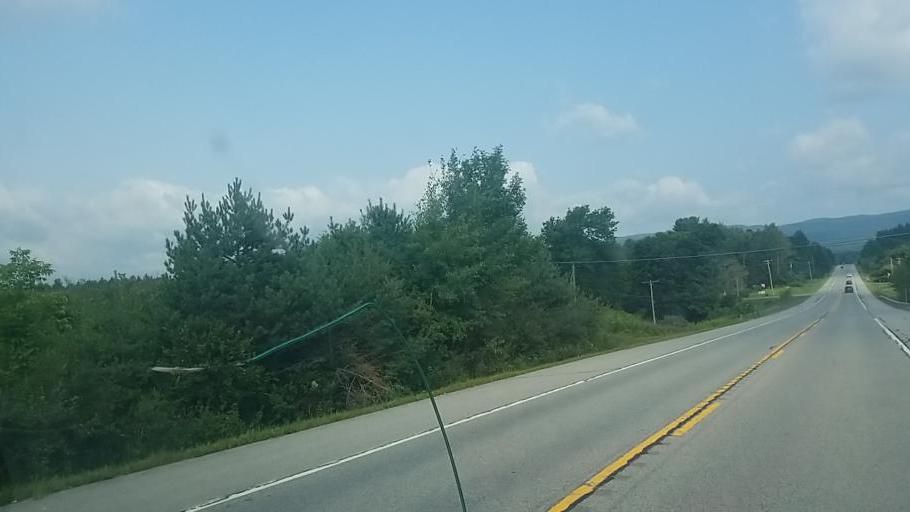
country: US
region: New York
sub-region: Fulton County
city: Broadalbin
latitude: 43.0864
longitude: -74.2698
